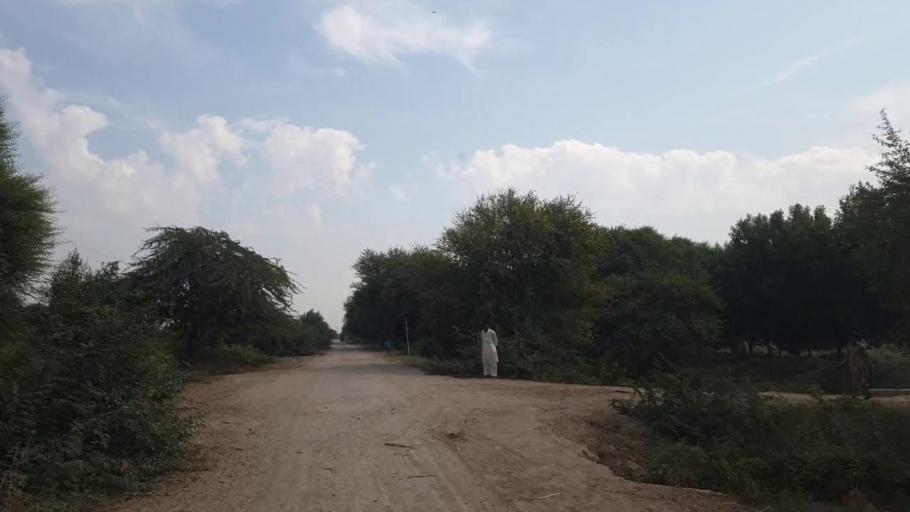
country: PK
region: Sindh
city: Tando Bago
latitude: 24.9251
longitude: 69.0176
